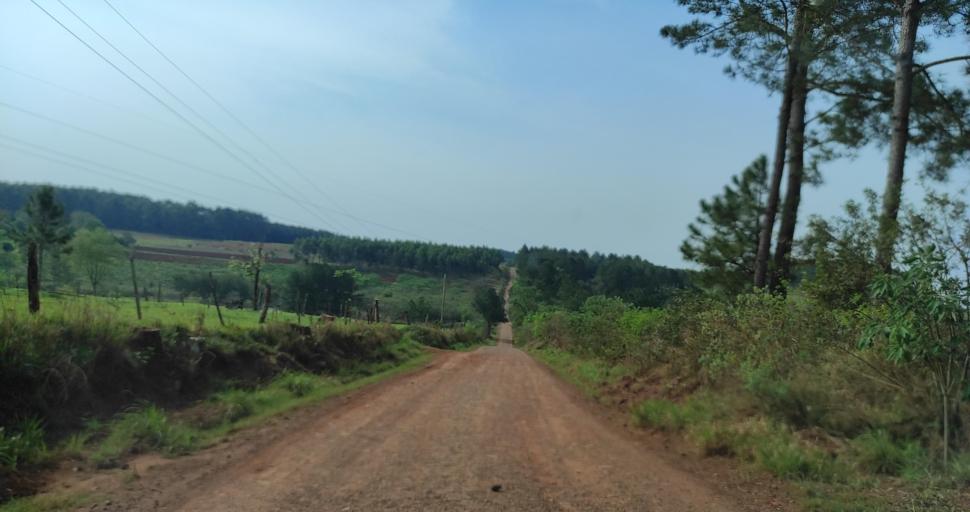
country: AR
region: Misiones
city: Garuhape
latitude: -26.8733
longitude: -55.0058
